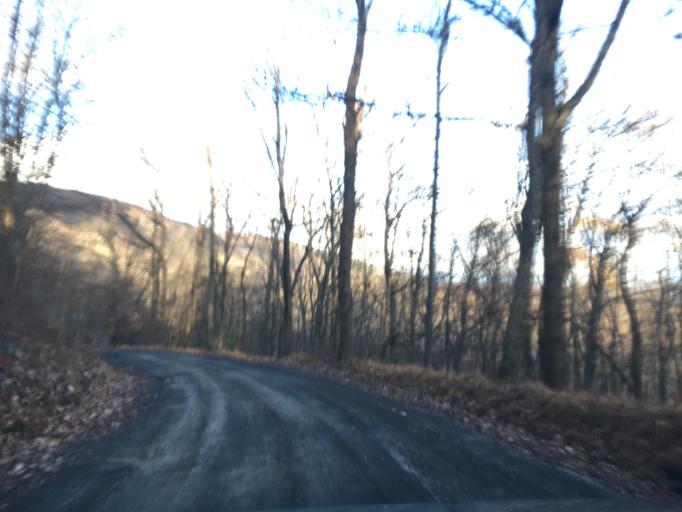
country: US
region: Pennsylvania
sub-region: Carbon County
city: Lehighton
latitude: 40.7637
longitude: -75.6948
